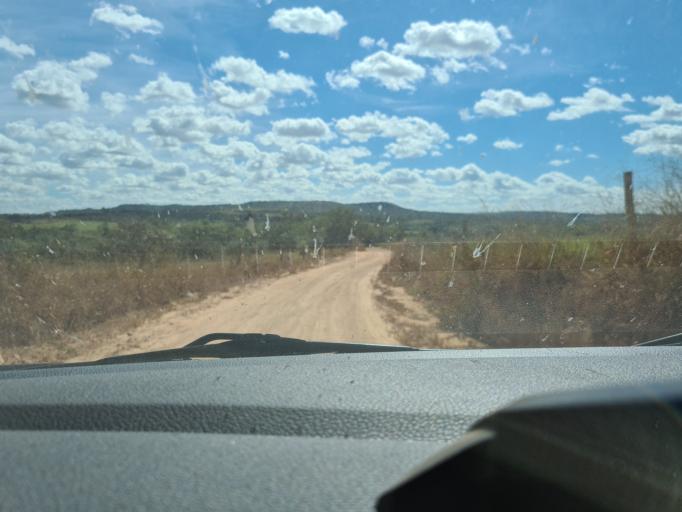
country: BR
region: Goias
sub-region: Silvania
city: Silvania
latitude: -16.5382
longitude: -48.5799
